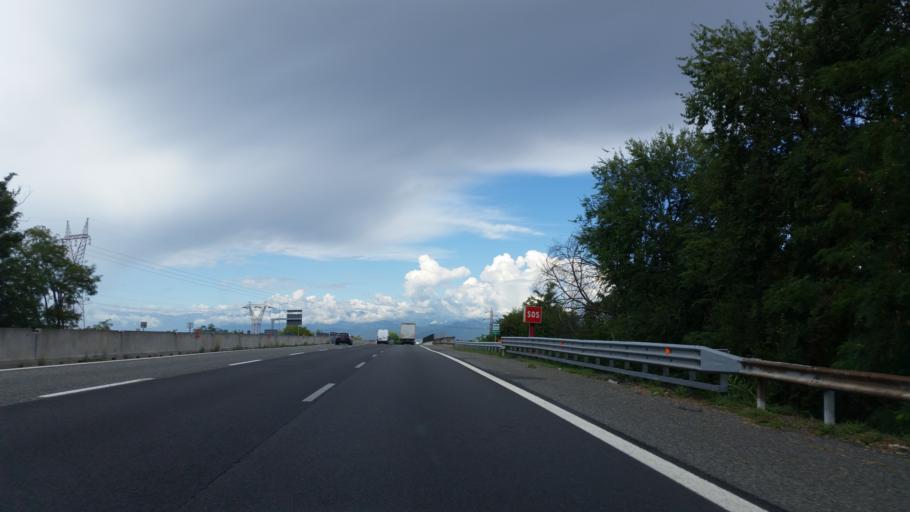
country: IT
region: Piedmont
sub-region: Provincia di Torino
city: Cambiano
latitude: 44.9598
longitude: 7.7819
